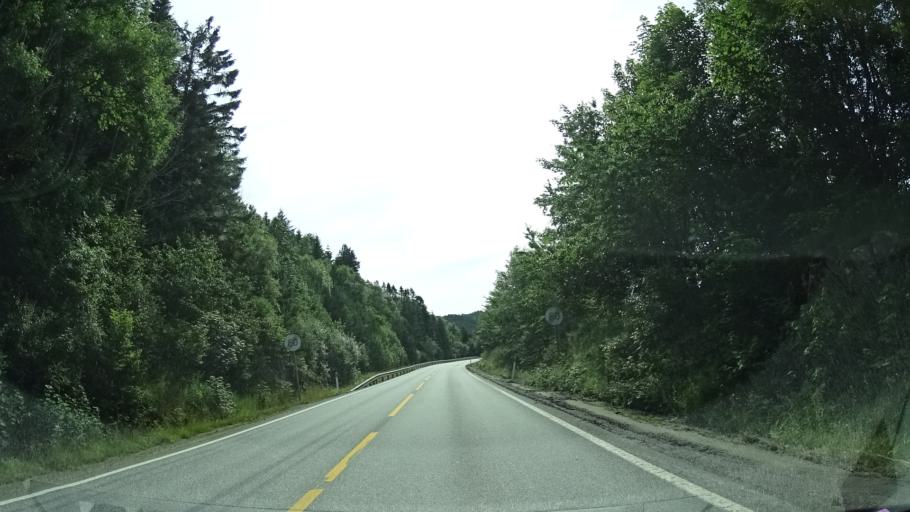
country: NO
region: Hordaland
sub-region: Bomlo
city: Mosterhamn
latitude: 59.6677
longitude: 5.4644
